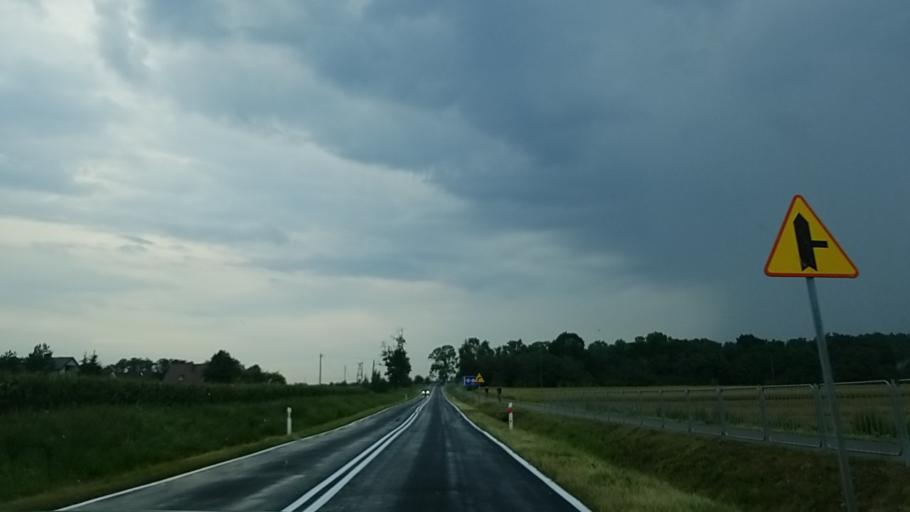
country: PL
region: Lublin Voivodeship
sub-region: Powiat wlodawski
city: Wlodawa
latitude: 51.6043
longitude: 23.5318
